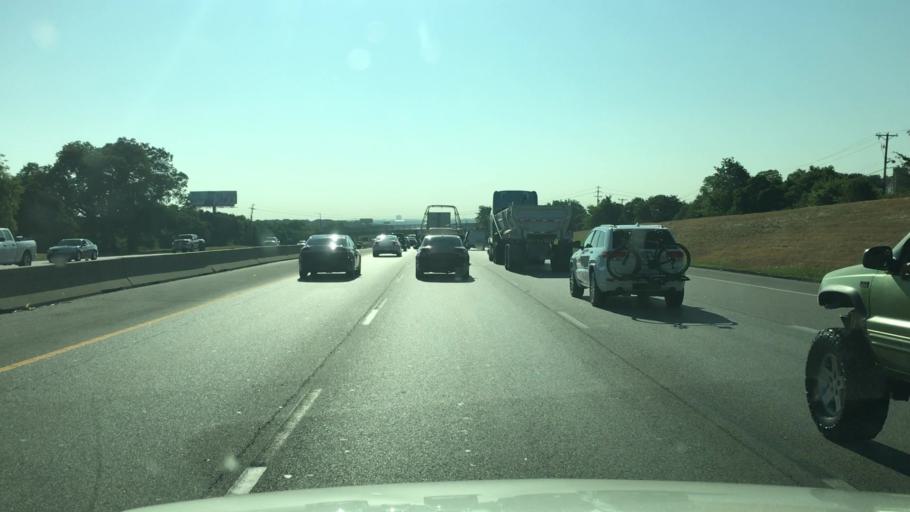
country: US
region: Texas
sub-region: Tarrant County
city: Richland Hills
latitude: 32.7597
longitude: -97.2013
